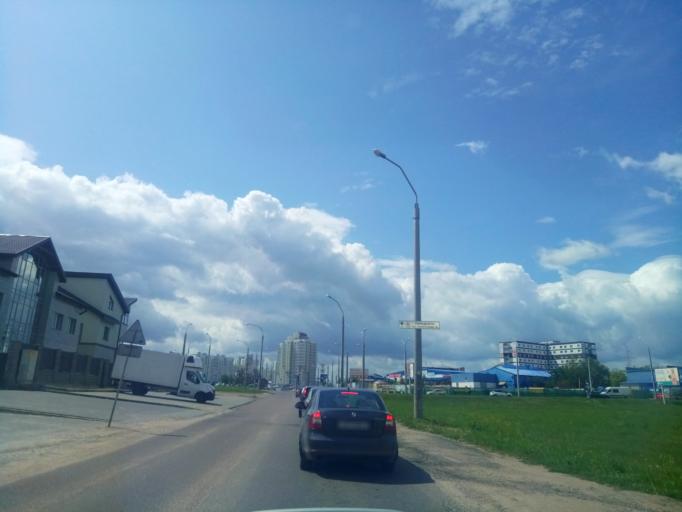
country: BY
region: Minsk
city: Zhdanovichy
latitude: 53.9365
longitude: 27.4329
